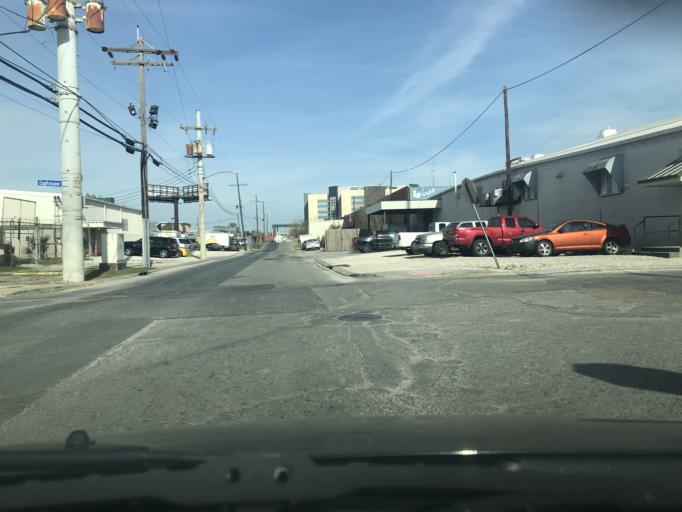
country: US
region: Louisiana
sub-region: Orleans Parish
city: New Orleans
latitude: 29.9572
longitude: -90.0981
